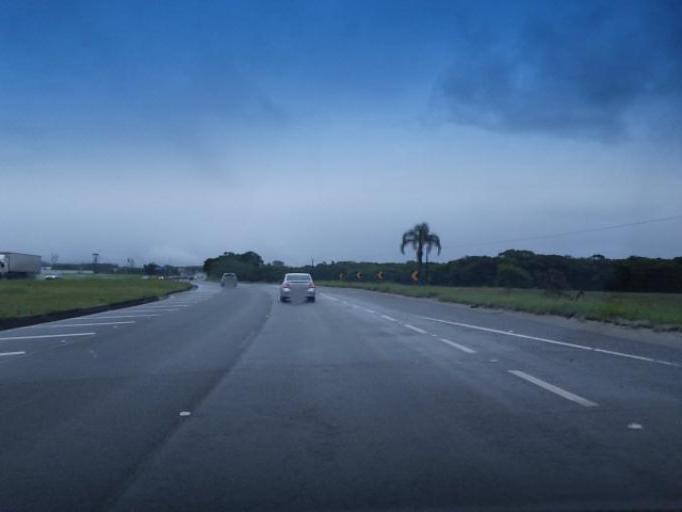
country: BR
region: Santa Catarina
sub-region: Barra Velha
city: Barra Velha
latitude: -26.4813
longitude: -48.7359
